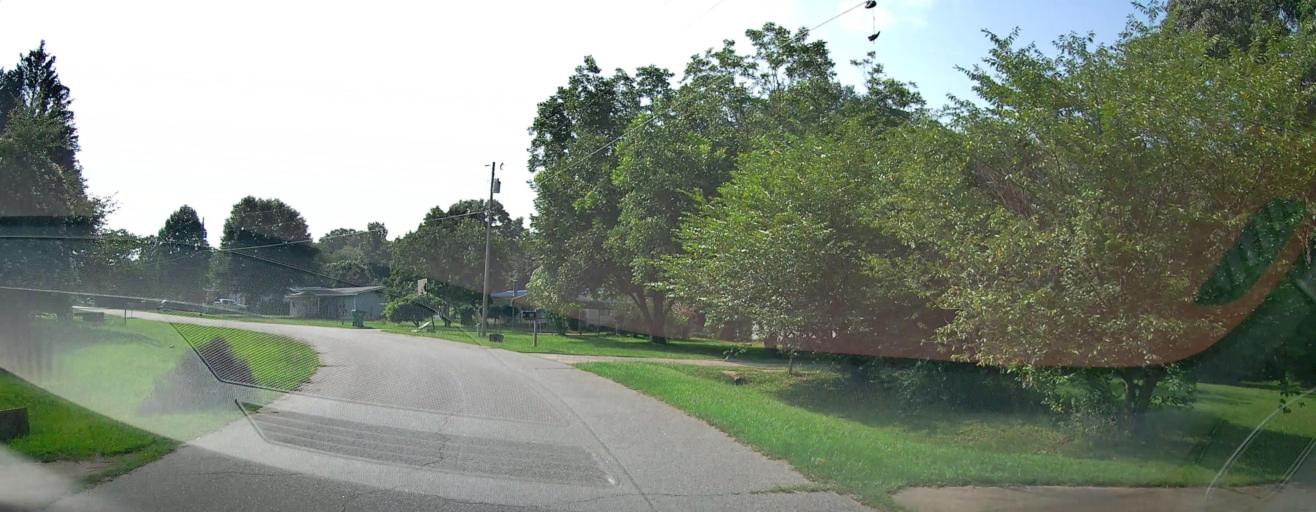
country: US
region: Georgia
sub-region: Houston County
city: Centerville
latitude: 32.6470
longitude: -83.6829
